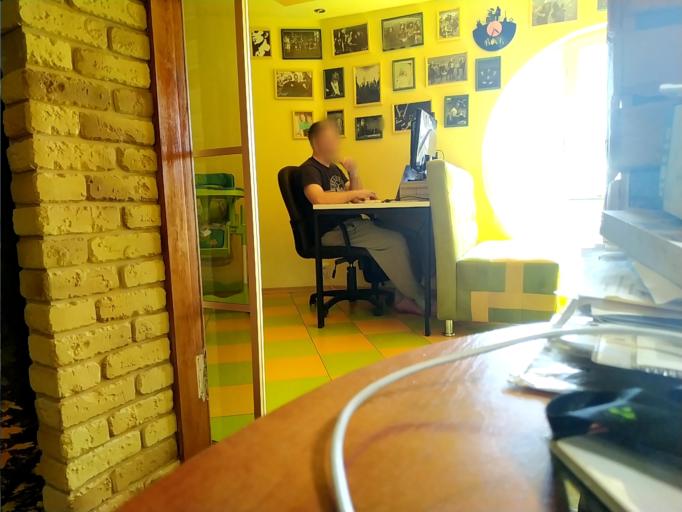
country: RU
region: Moskovskaya
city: Rakhmanovo
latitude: 55.7389
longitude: 38.5989
